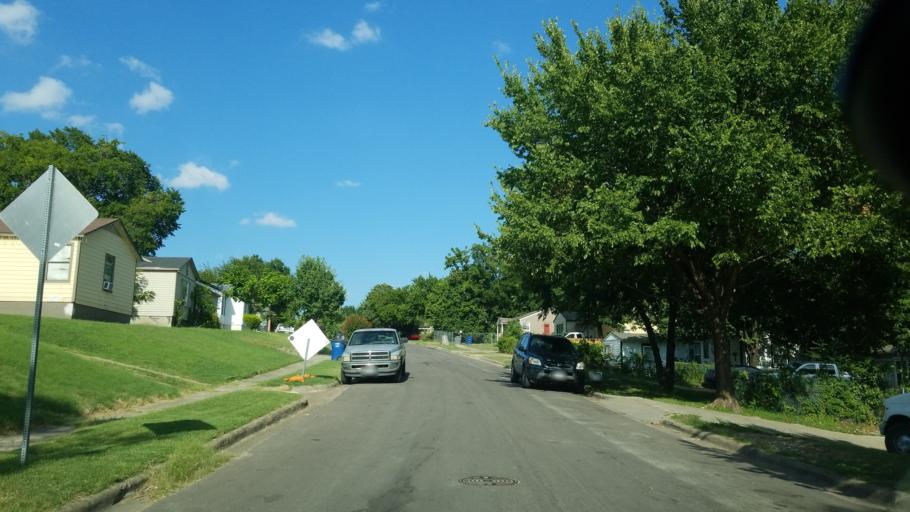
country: US
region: Texas
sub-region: Dallas County
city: Dallas
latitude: 32.7661
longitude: -96.7124
